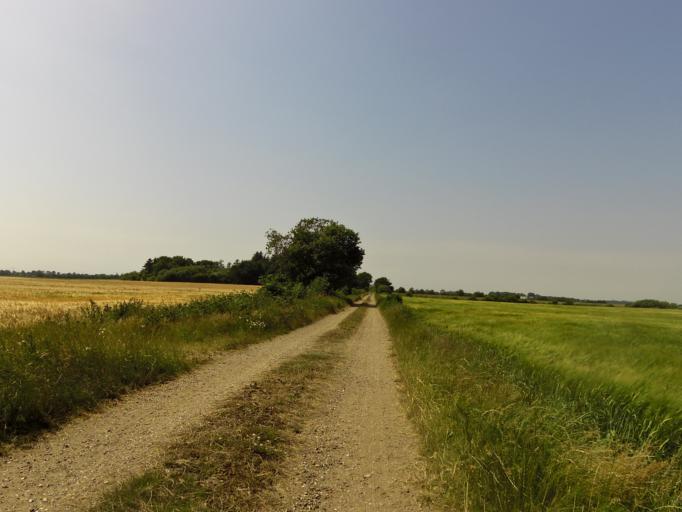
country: DK
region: South Denmark
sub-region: Aabenraa Kommune
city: Rodekro
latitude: 55.1427
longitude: 9.2366
